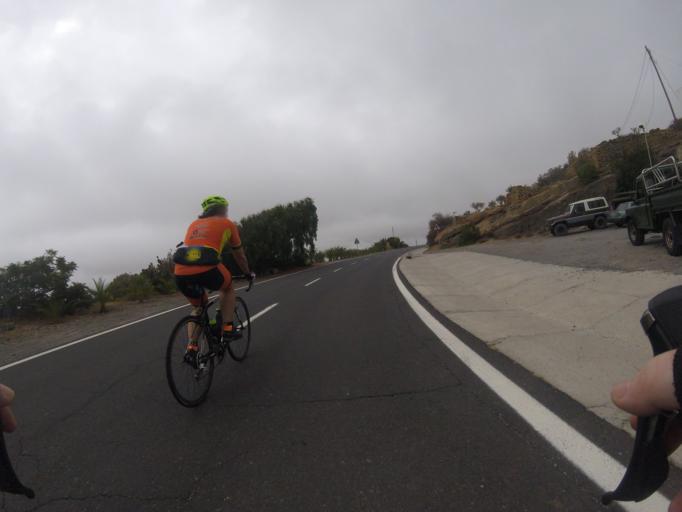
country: ES
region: Canary Islands
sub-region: Provincia de Santa Cruz de Tenerife
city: Fasnia
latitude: 28.2070
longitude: -16.4532
